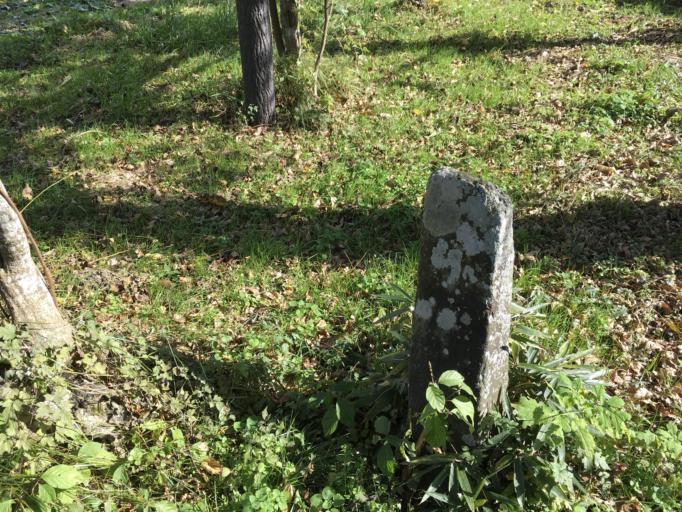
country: JP
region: Iwate
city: Ichinoseki
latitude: 38.9555
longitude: 141.3705
